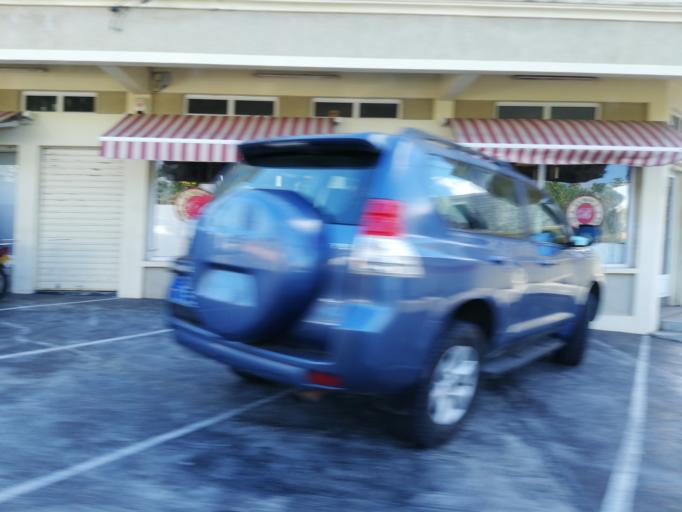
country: MU
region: Riviere du Rempart
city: Grand Baie
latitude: -20.0184
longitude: 57.5857
